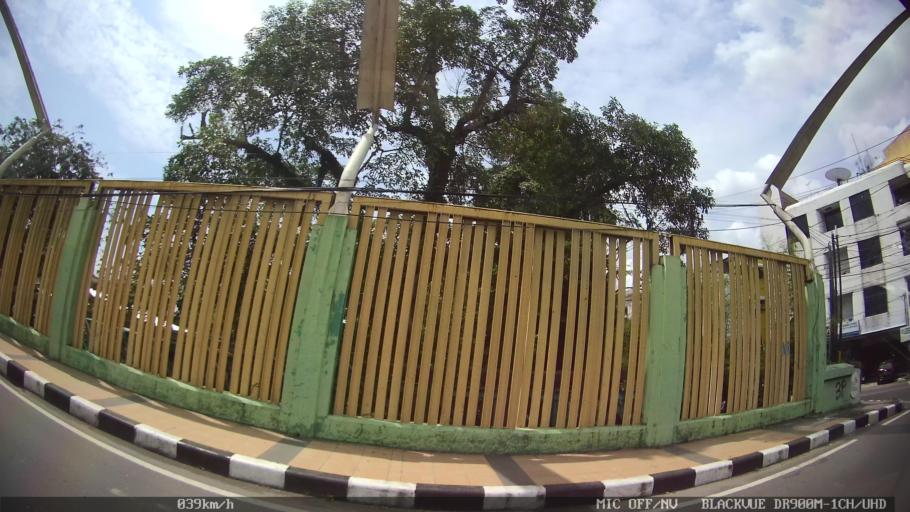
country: ID
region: North Sumatra
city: Medan
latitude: 3.5805
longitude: 98.6804
